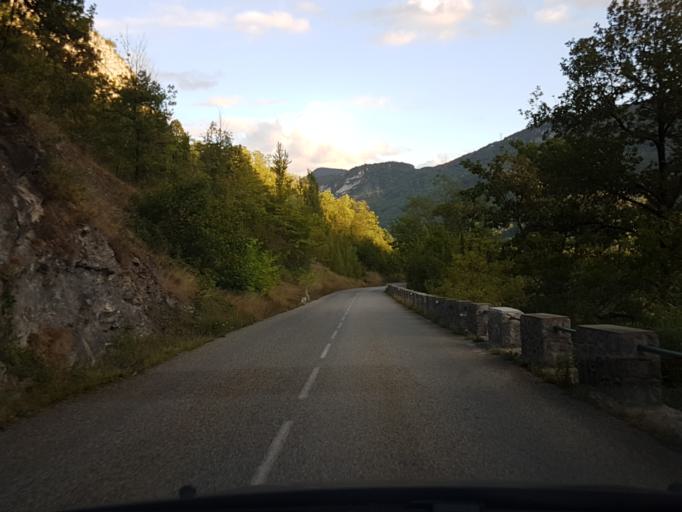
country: FR
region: Midi-Pyrenees
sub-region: Departement de l'Ariege
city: Tarascon-sur-Ariege
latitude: 42.8671
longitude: 1.5687
